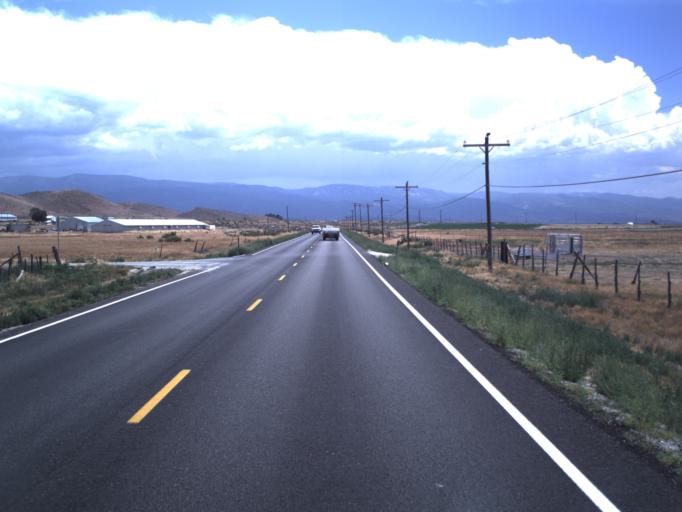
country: US
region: Utah
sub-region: Sanpete County
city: Moroni
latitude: 39.5648
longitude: -111.6043
